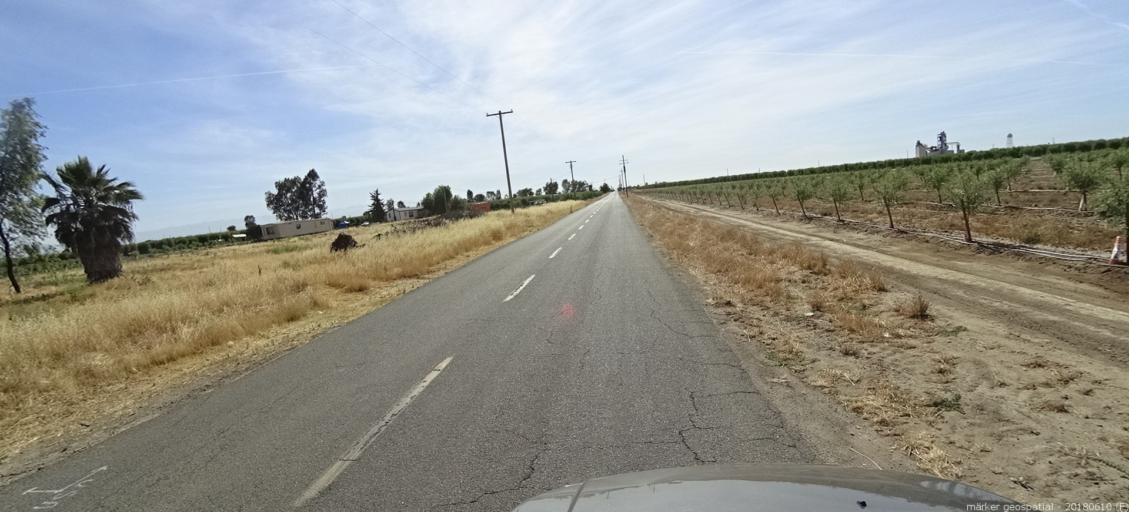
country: US
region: California
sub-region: Madera County
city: Chowchilla
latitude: 37.0983
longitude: -120.2365
